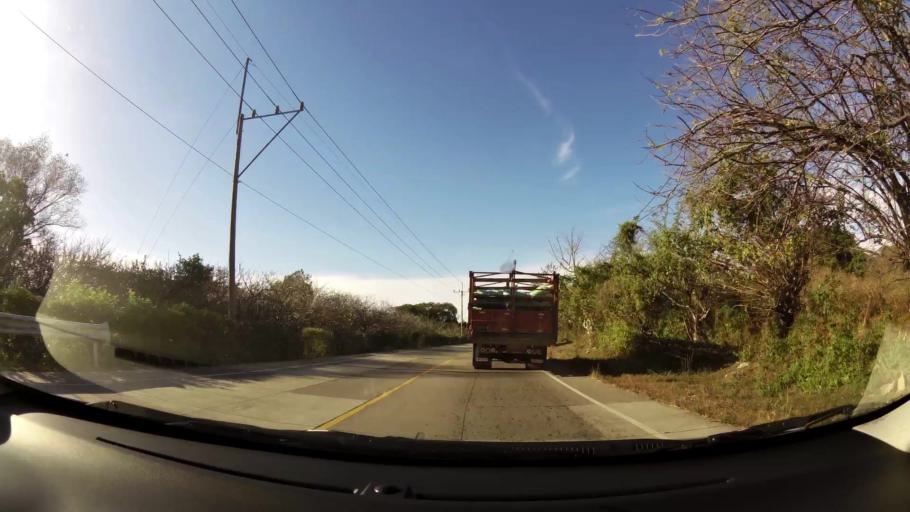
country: SV
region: Santa Ana
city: Metapan
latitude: 14.2387
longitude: -89.4713
